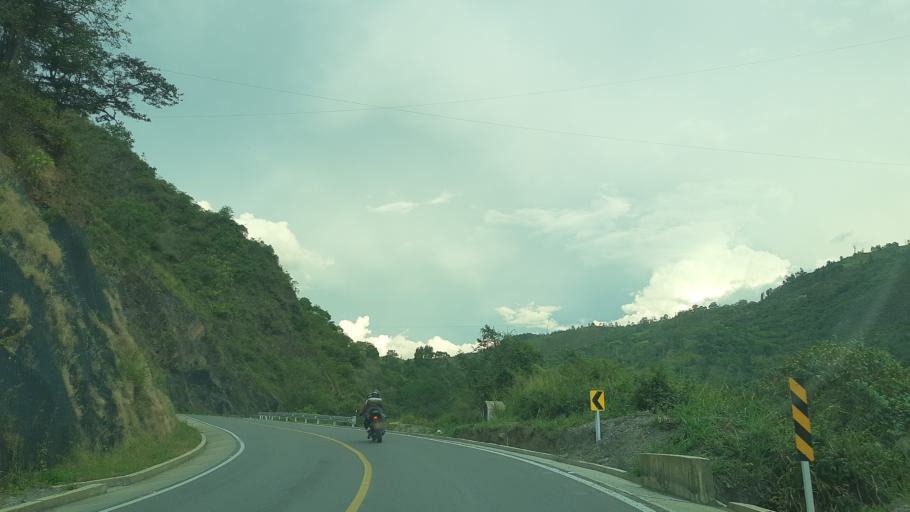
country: CO
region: Boyaca
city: Somondoco
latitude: 5.0082
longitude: -73.4057
